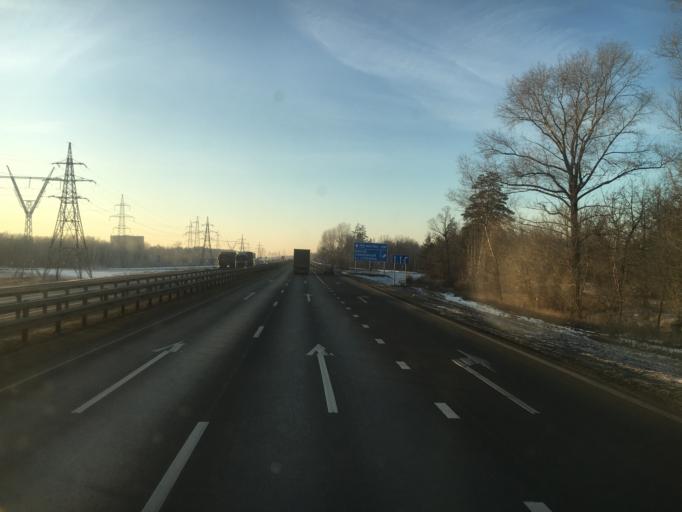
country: RU
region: Samara
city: Pribrezhnyy
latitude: 53.5171
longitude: 49.8443
